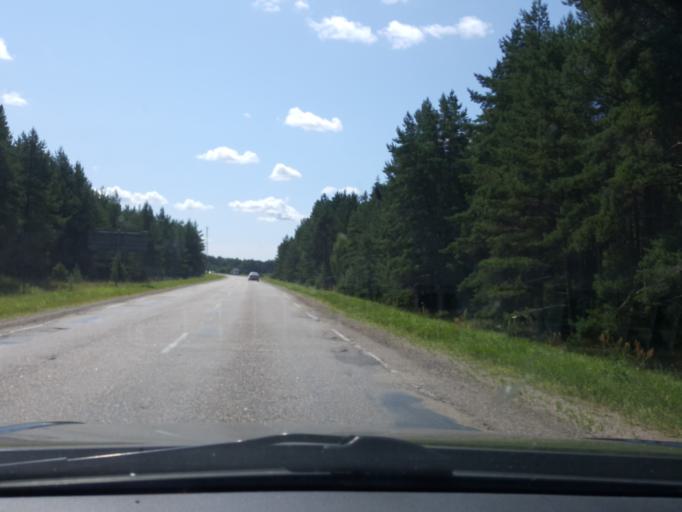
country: LT
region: Klaipedos apskritis
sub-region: Palanga
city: Sventoji
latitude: 56.0868
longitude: 21.1245
